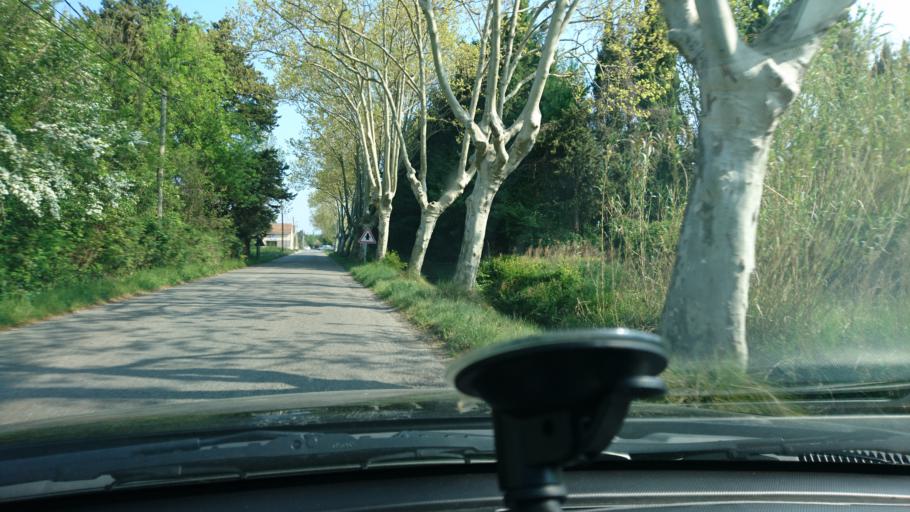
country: FR
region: Provence-Alpes-Cote d'Azur
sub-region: Departement des Bouches-du-Rhone
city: Noves
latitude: 43.8414
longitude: 4.8991
